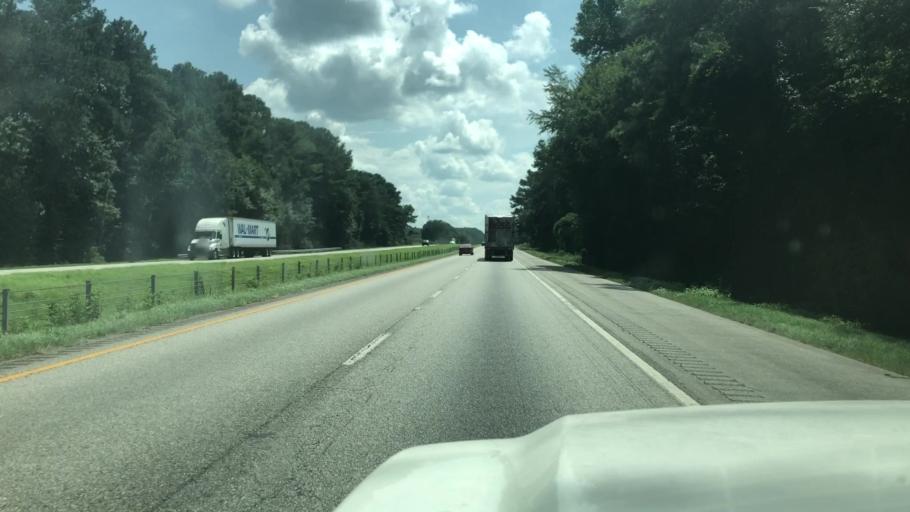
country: US
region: Alabama
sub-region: Chambers County
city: Huguley
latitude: 32.8015
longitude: -85.2313
